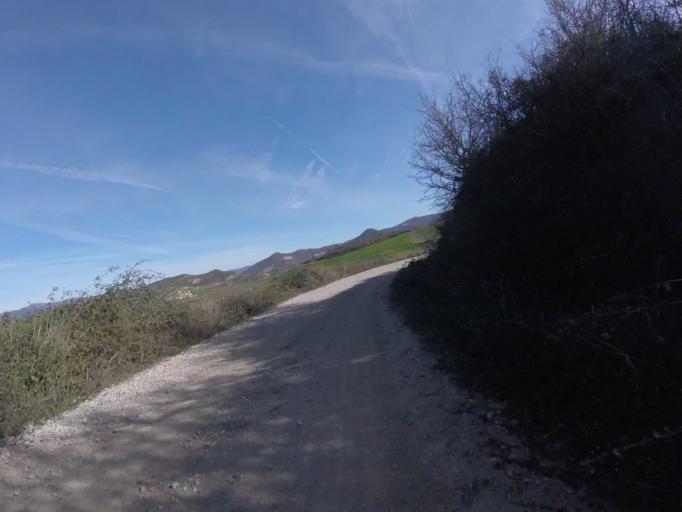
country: ES
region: Navarre
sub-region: Provincia de Navarra
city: Yerri
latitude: 42.6820
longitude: -1.9643
